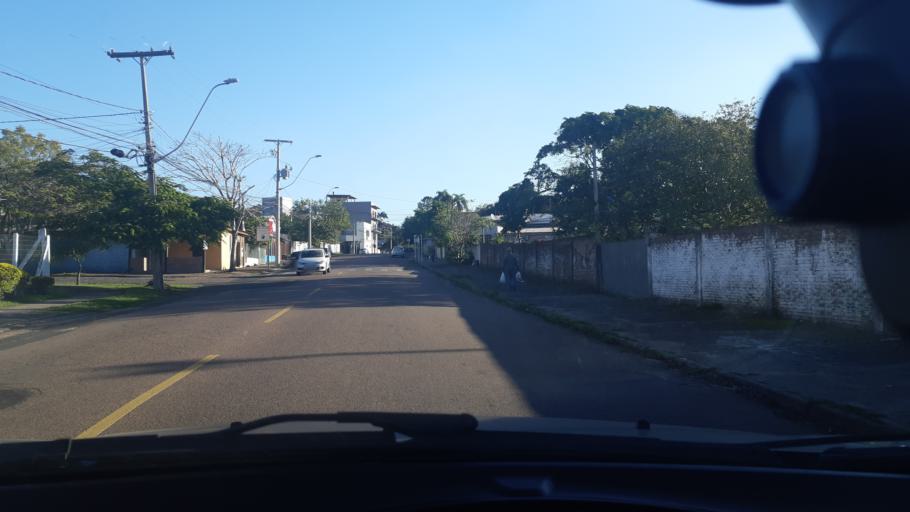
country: BR
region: Rio Grande do Sul
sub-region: Sao Leopoldo
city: Sao Leopoldo
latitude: -29.7777
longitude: -51.1303
